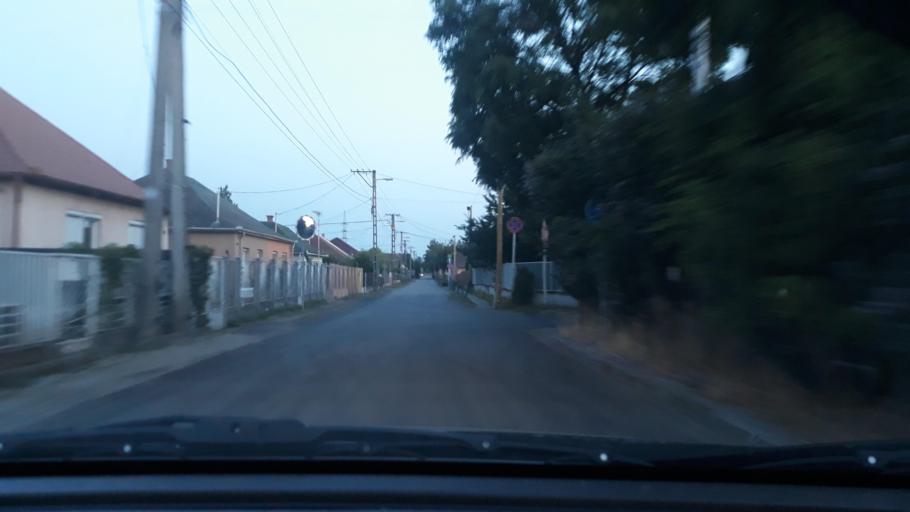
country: HU
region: Hajdu-Bihar
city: Debrecen
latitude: 47.5341
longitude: 21.6660
